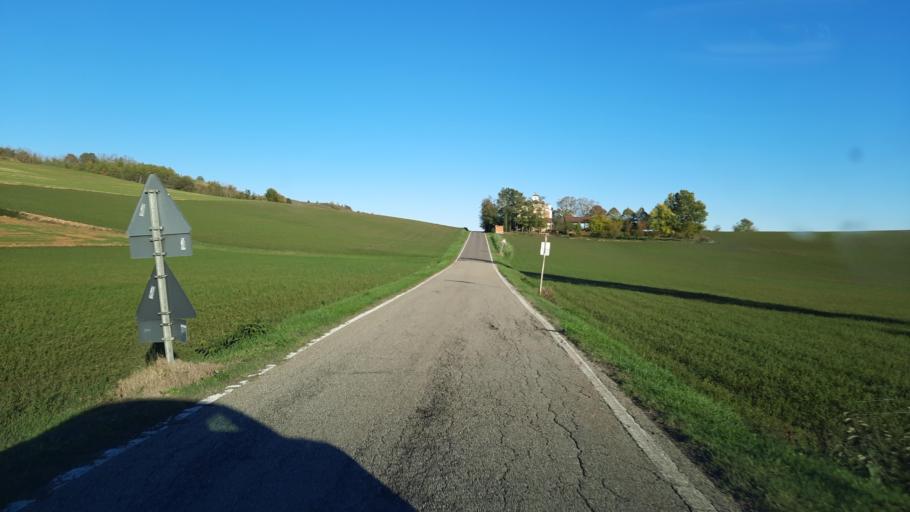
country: IT
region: Piedmont
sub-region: Provincia di Alessandria
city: Cuccaro Monferrato
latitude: 44.9871
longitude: 8.4684
